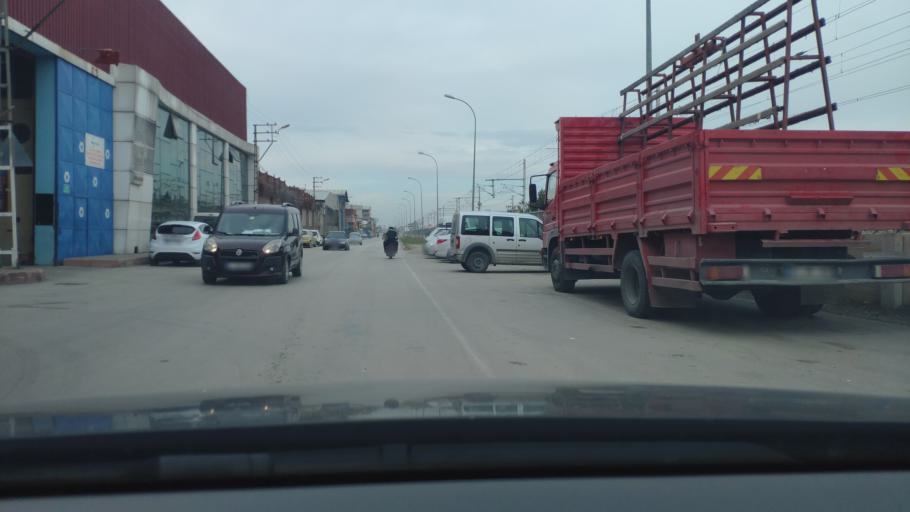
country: TR
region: Adana
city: Seyhan
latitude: 36.9974
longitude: 35.2731
